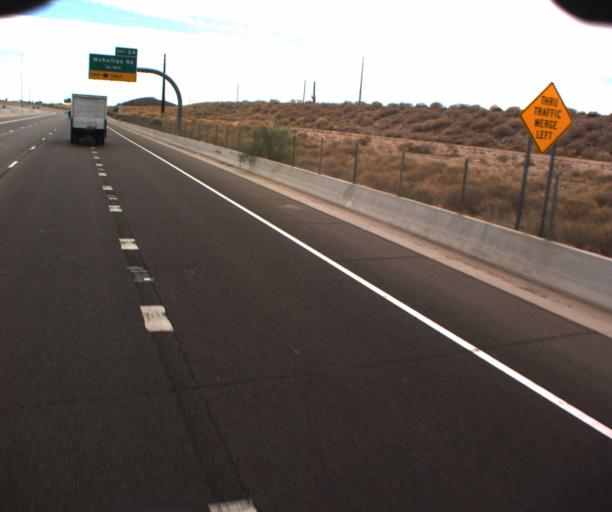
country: US
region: Arizona
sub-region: Pinal County
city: Apache Junction
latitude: 33.4604
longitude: -111.6769
